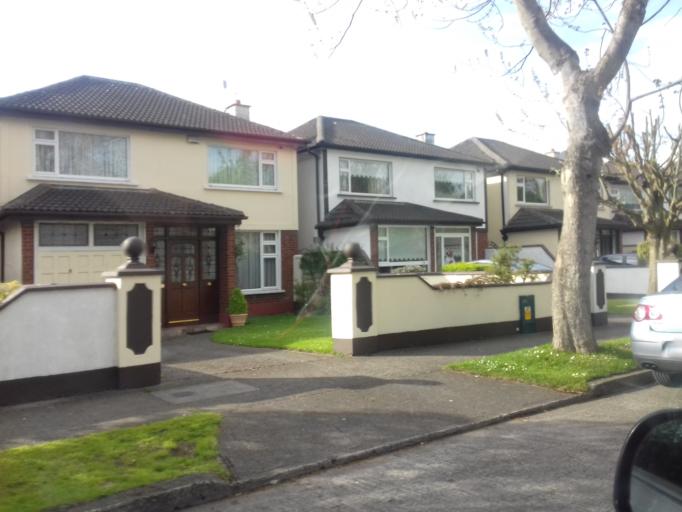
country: IE
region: Leinster
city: Castleknock
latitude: 53.3745
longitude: -6.3657
